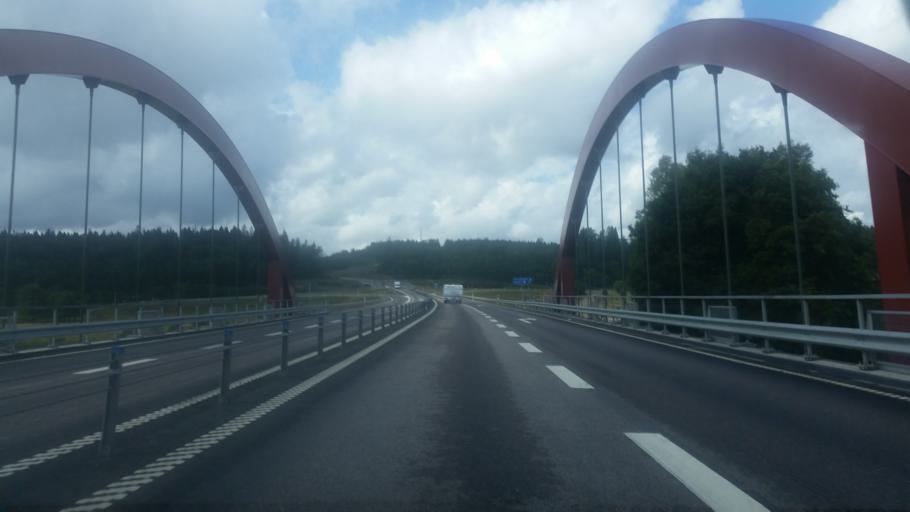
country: SE
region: Vaestra Goetaland
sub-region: Boras Kommun
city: Boras
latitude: 57.6972
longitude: 12.9130
